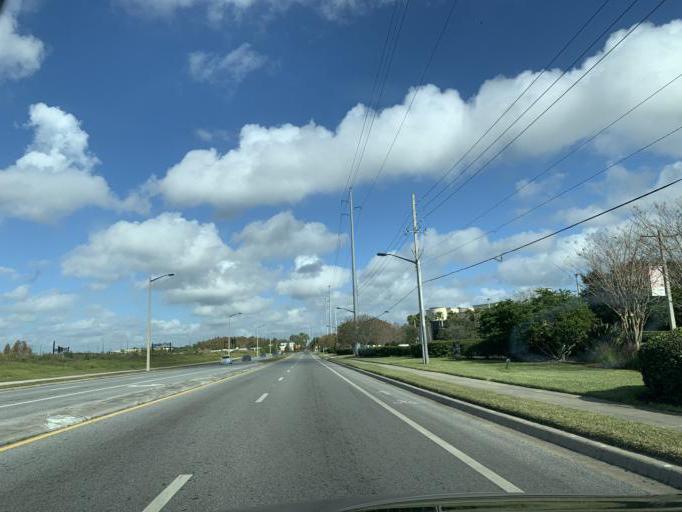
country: US
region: Florida
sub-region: Orange County
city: Oak Ridge
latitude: 28.4796
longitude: -81.4422
